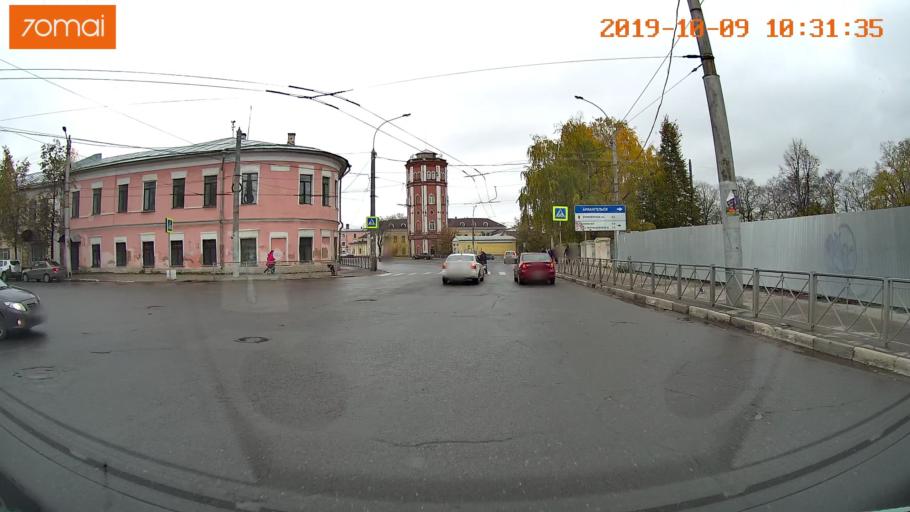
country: RU
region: Vologda
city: Vologda
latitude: 59.2225
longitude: 39.8917
